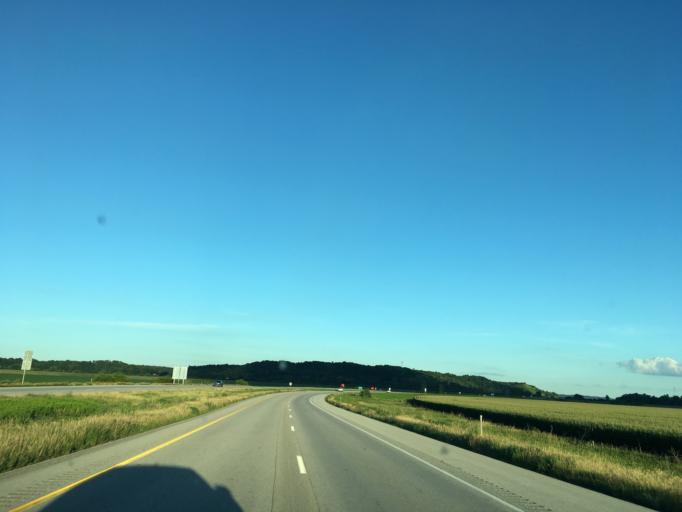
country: US
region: Iowa
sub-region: Fremont County
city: Hamburg
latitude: 40.5856
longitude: -95.6549
